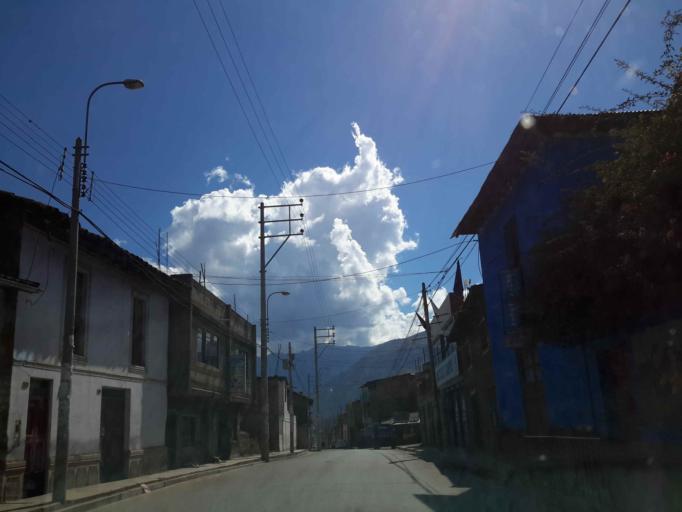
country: PE
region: Apurimac
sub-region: Provincia de Andahuaylas
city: Talavera
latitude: -13.6546
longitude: -73.4248
